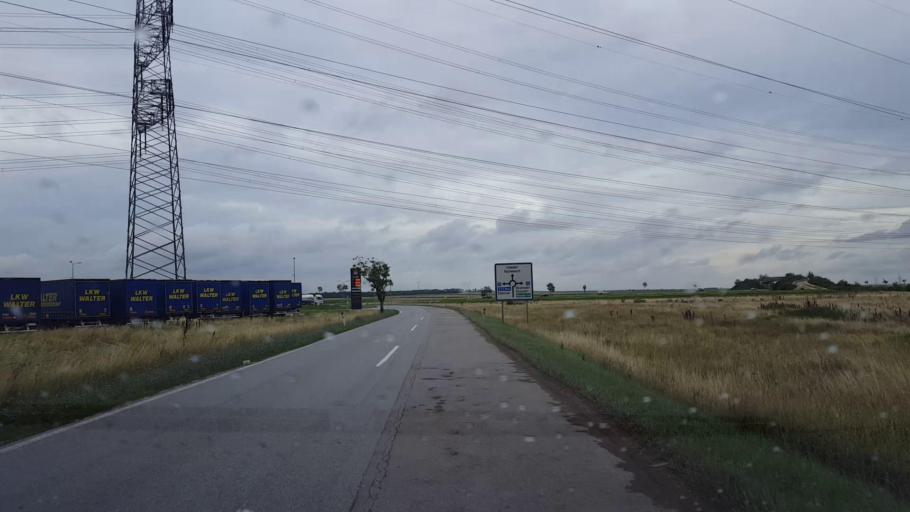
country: AT
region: Lower Austria
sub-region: Politischer Bezirk Wien-Umgebung
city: Himberg
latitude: 48.0829
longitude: 16.4548
